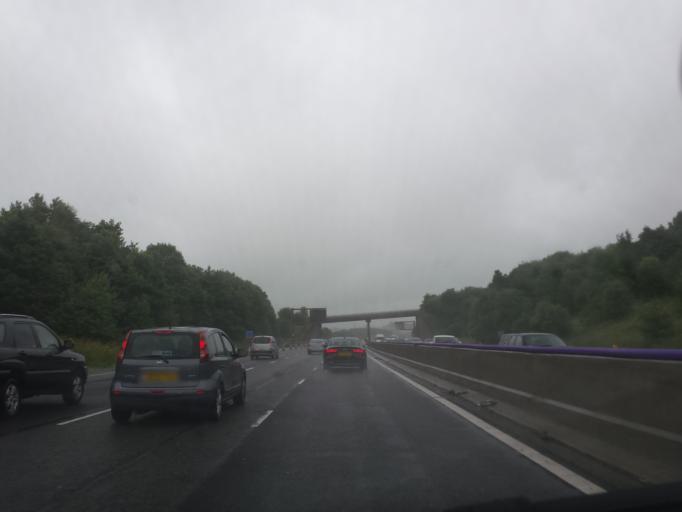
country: GB
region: England
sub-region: Derbyshire
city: Tibshelf
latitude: 53.1667
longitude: -1.3241
